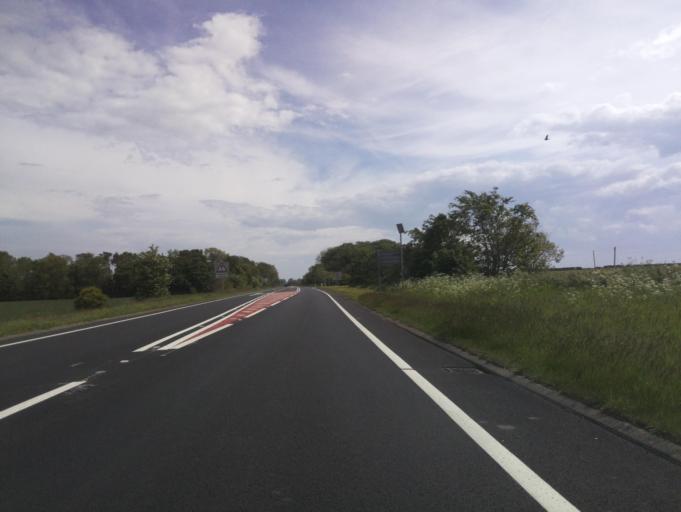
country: GB
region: England
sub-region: Northumberland
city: Ellingham
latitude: 55.4761
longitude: -1.7198
